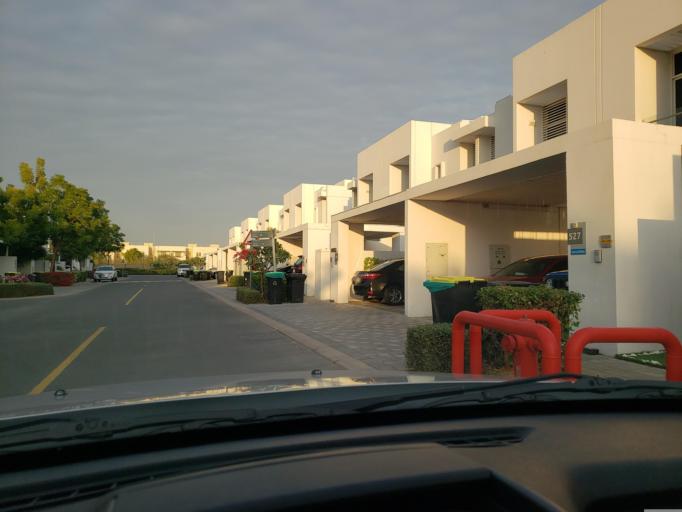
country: AE
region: Dubai
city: Dubai
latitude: 25.0175
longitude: 55.2743
